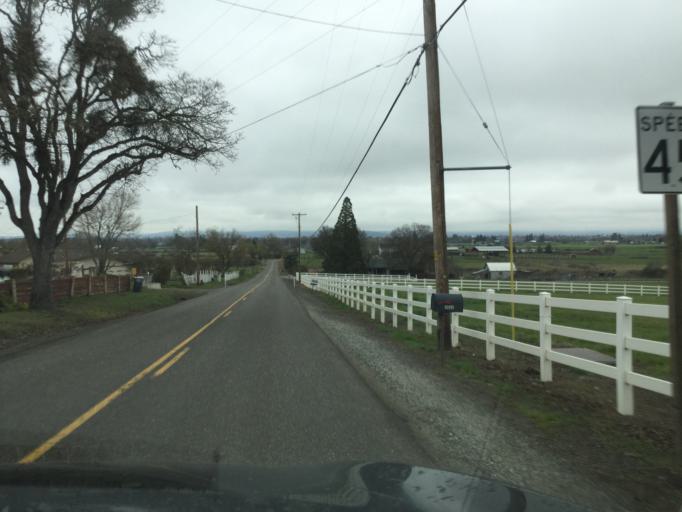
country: US
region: Oregon
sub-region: Jackson County
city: Central Point
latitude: 42.3902
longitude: -122.9578
